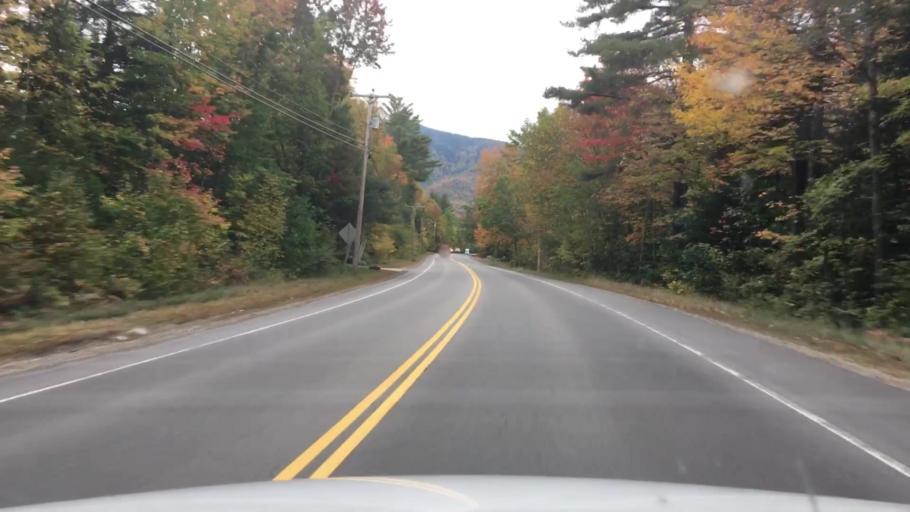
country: US
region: New Hampshire
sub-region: Coos County
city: Gorham
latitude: 44.3740
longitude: -71.1747
